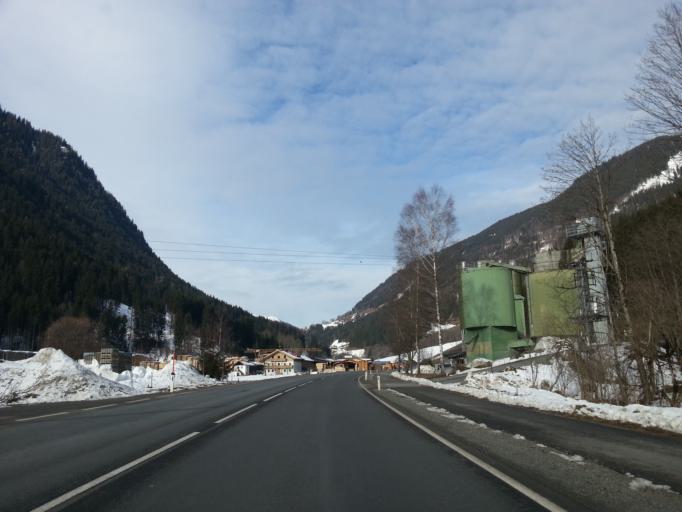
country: AT
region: Salzburg
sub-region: Politischer Bezirk Zell am See
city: Maishofen
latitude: 47.3637
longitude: 12.7876
